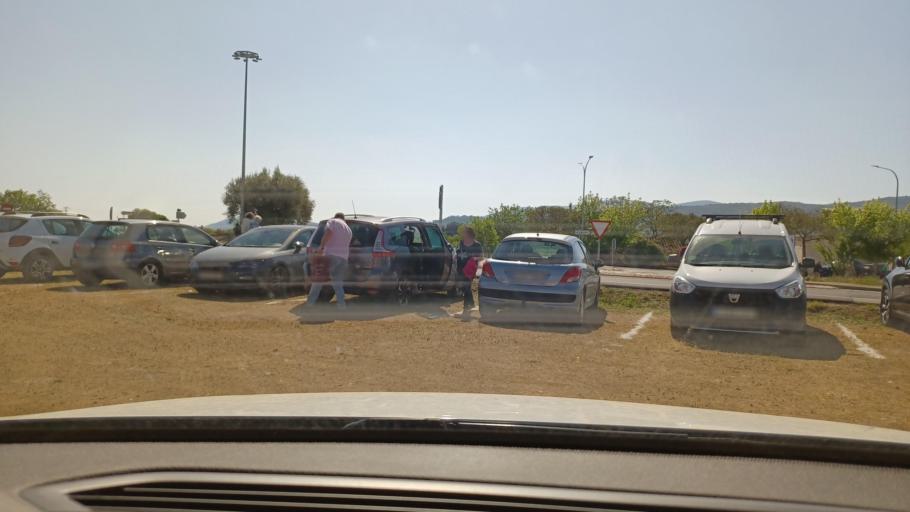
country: ES
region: Catalonia
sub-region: Provincia de Tarragona
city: Santa Barbara
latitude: 40.6858
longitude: 0.4637
